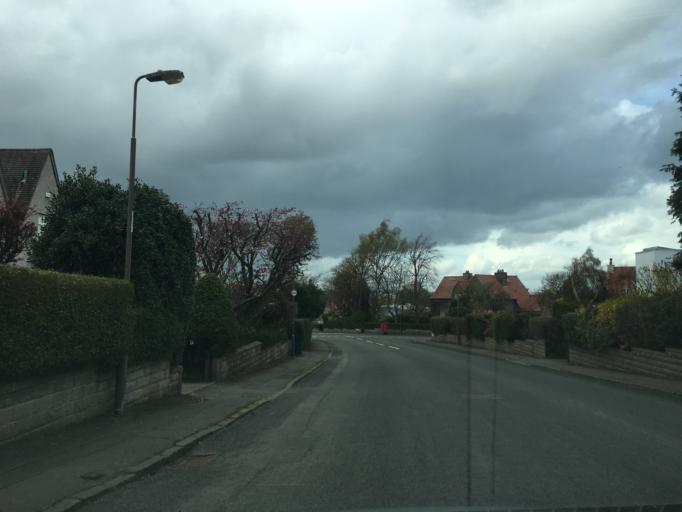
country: GB
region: Scotland
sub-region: Edinburgh
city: Edinburgh
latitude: 55.9170
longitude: -3.2093
